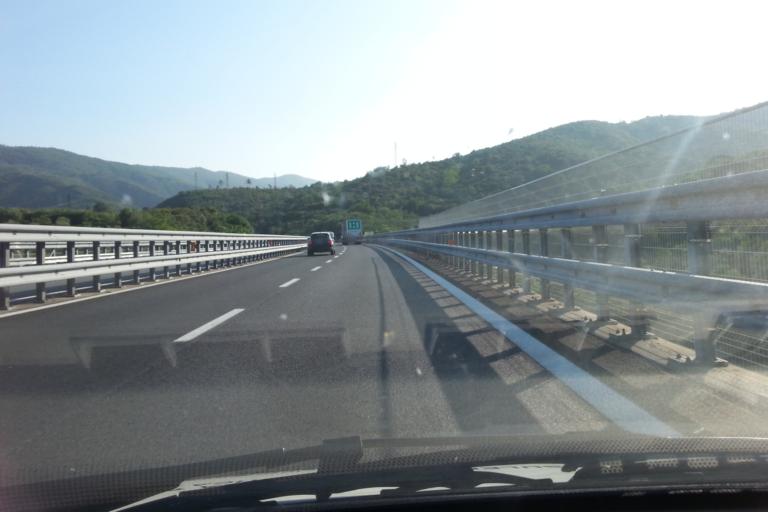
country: IT
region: Liguria
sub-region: Provincia di Savona
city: Valle di Vado
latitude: 44.2639
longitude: 8.4110
